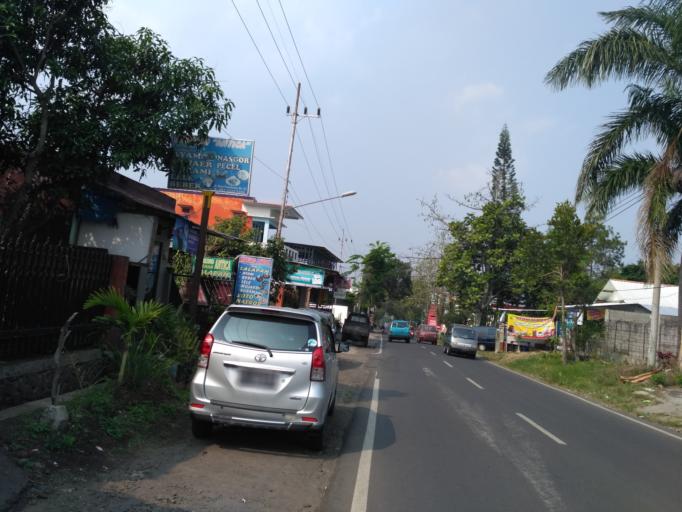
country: ID
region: East Java
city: Batu
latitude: -7.8647
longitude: 112.5413
